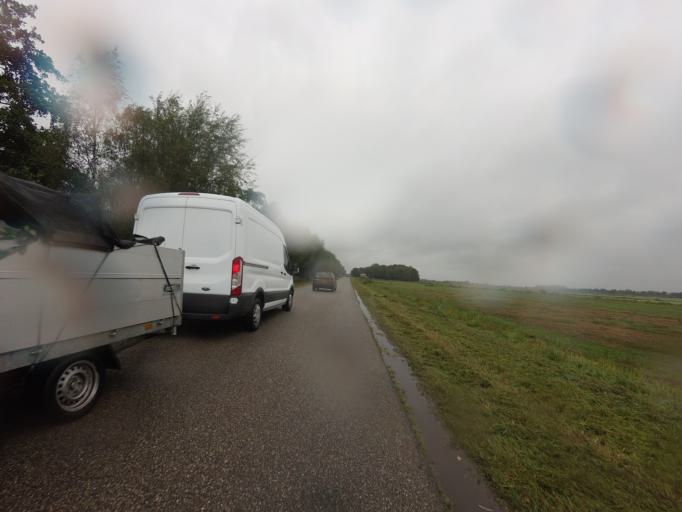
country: NL
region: Friesland
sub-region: Gemeente Tytsjerksteradiel
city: Garyp
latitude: 53.1331
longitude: 5.9566
